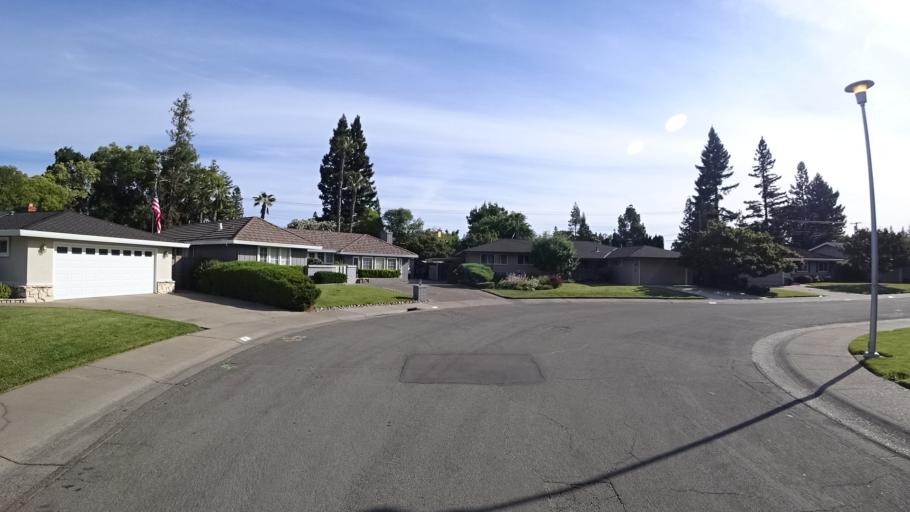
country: US
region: California
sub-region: Sacramento County
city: Arden-Arcade
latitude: 38.5707
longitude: -121.3996
